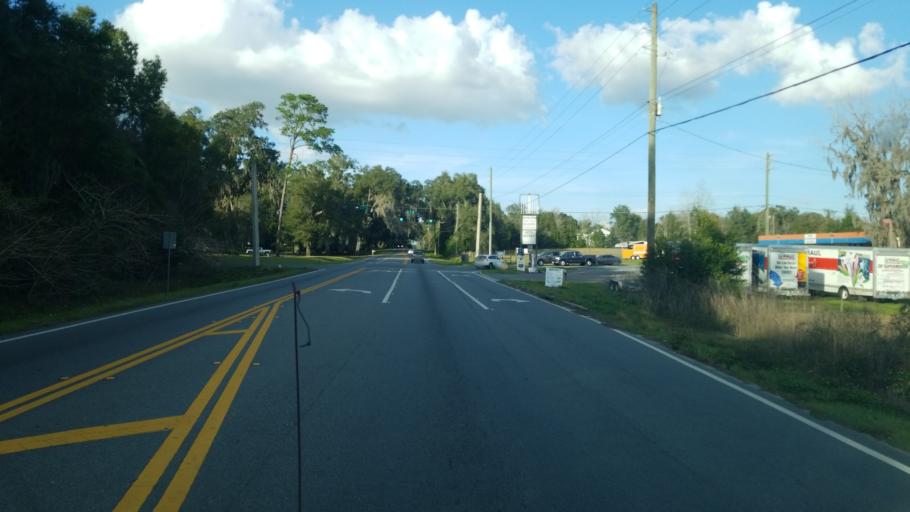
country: US
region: Florida
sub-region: Marion County
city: Ocala
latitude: 29.2369
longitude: -82.1200
